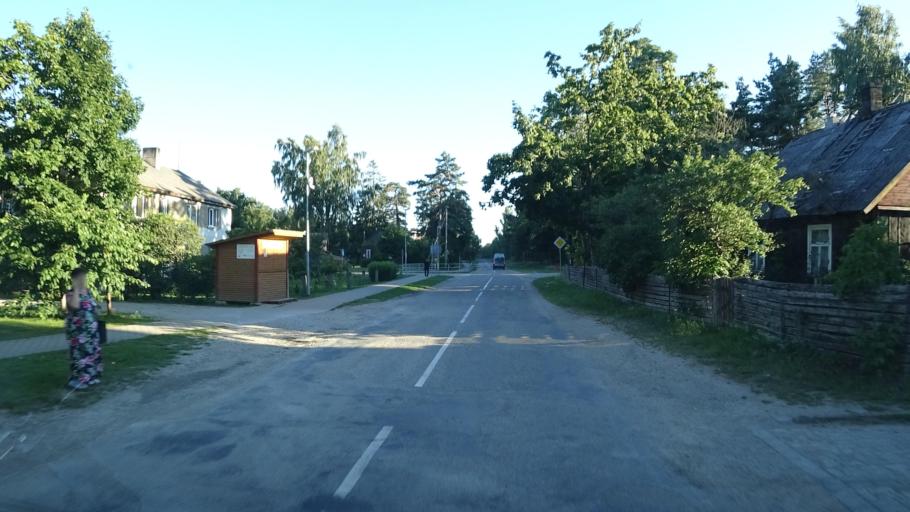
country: LV
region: Dundaga
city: Dundaga
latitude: 57.7379
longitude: 22.5822
